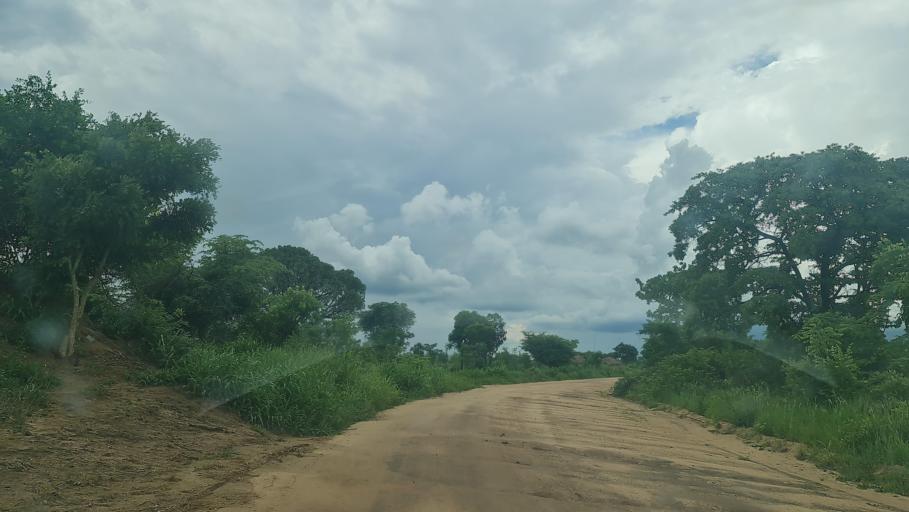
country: MW
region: Southern Region
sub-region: Nsanje District
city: Nsanje
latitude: -17.5866
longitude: 35.6675
